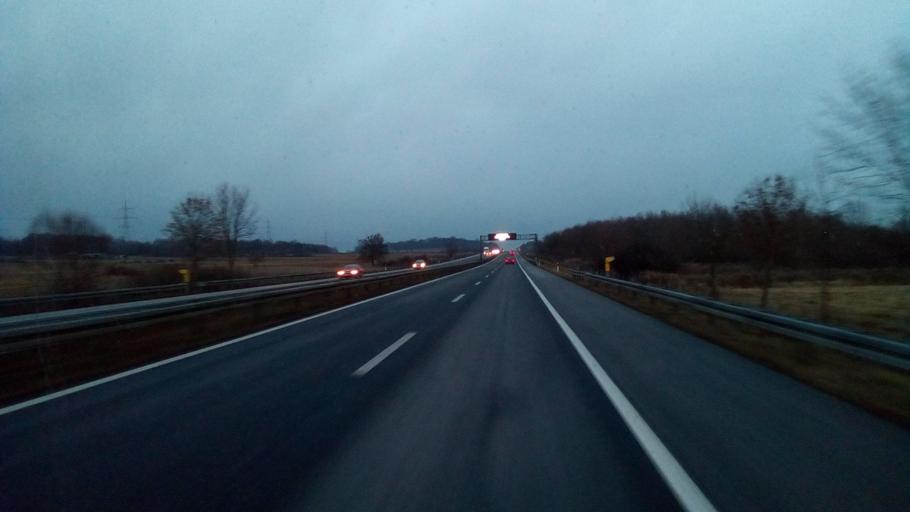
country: HR
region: Zagrebacka
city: Brckovljani
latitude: 45.8846
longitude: 16.2302
